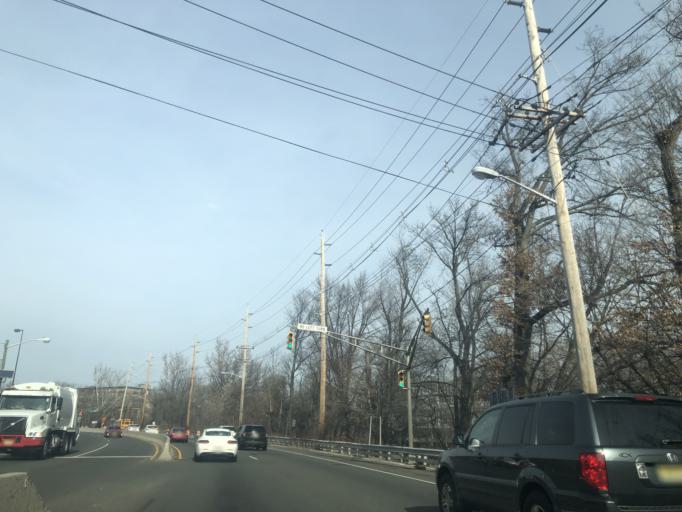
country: US
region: New Jersey
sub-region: Bergen County
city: Fair Lawn
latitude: 40.9323
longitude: -74.1406
